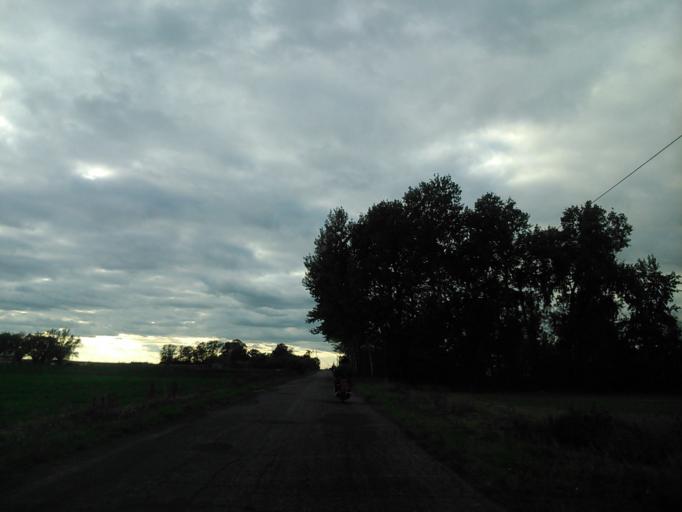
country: PL
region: Kujawsko-Pomorskie
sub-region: Powiat golubsko-dobrzynski
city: Kowalewo Pomorskie
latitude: 53.1196
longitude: 18.9017
